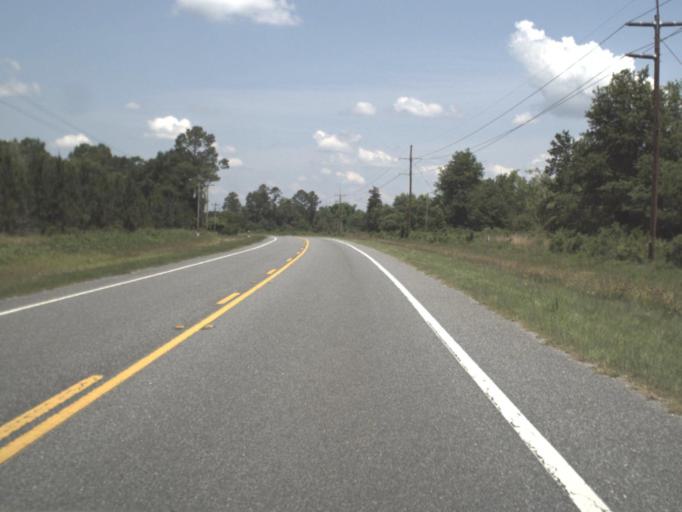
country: US
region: Florida
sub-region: Bradford County
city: Starke
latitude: 29.9535
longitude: -82.1483
